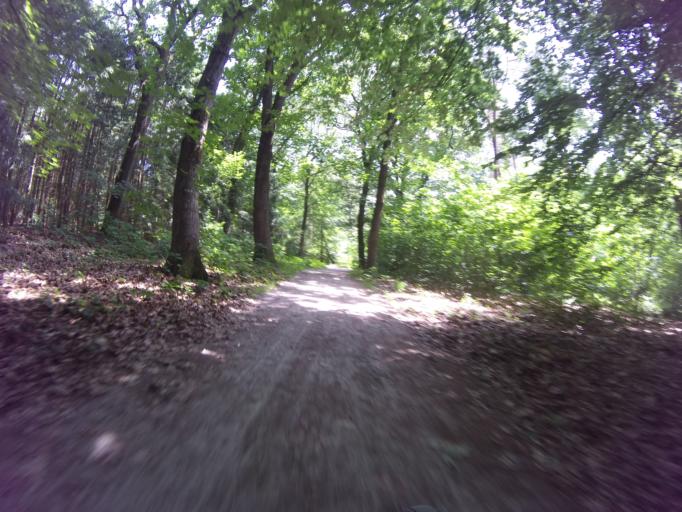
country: NL
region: Gelderland
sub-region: Gemeente Ede
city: Lunteren
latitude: 52.0818
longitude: 5.6478
